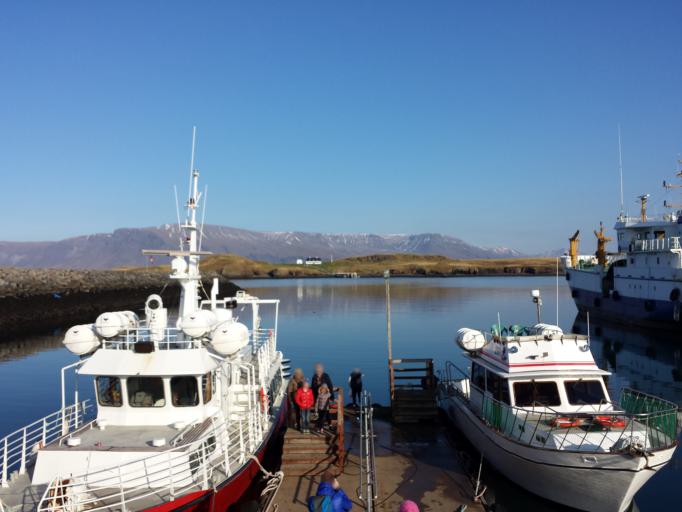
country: IS
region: Capital Region
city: Reykjavik
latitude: 64.1563
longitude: -21.8671
